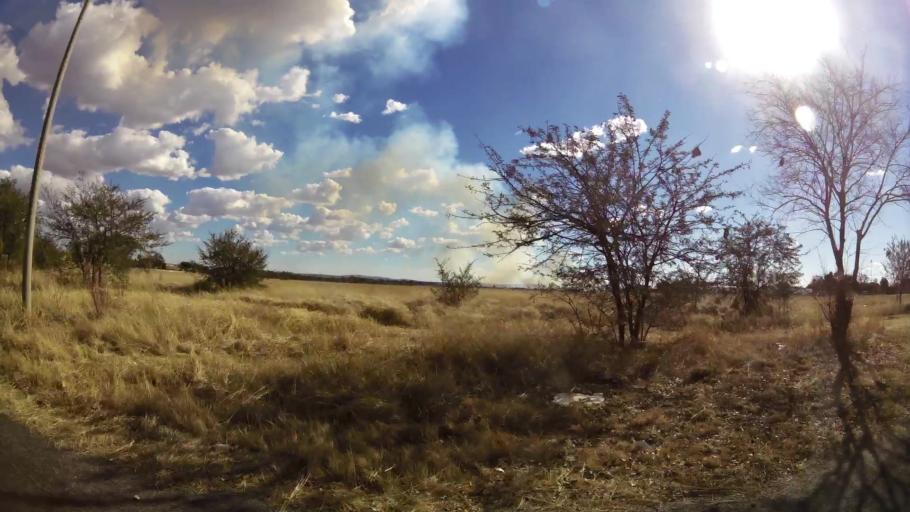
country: ZA
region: North-West
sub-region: Dr Kenneth Kaunda District Municipality
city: Klerksdorp
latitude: -26.8299
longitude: 26.6532
